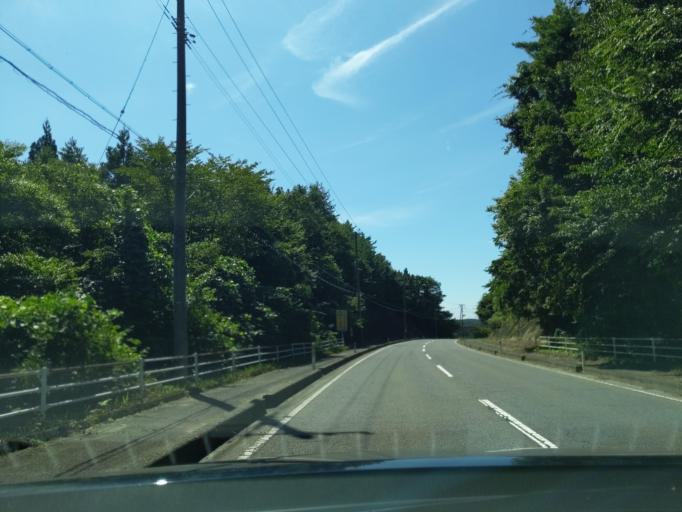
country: JP
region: Fukushima
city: Koriyama
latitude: 37.4090
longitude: 140.2707
